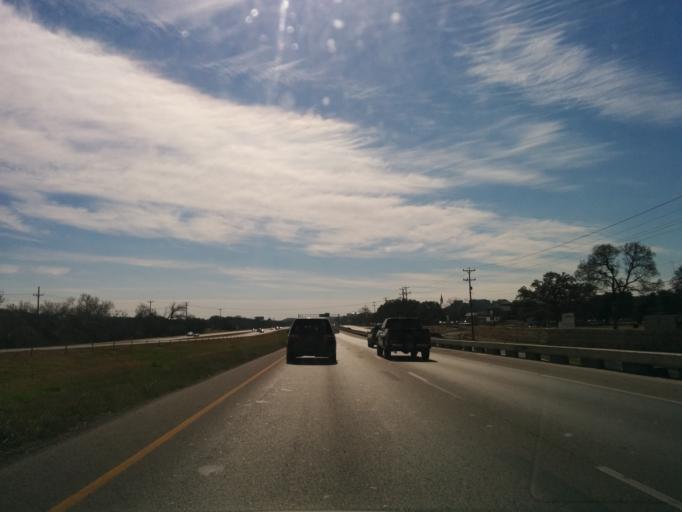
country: US
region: Texas
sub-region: Bexar County
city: Cross Mountain
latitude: 29.6462
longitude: -98.6213
